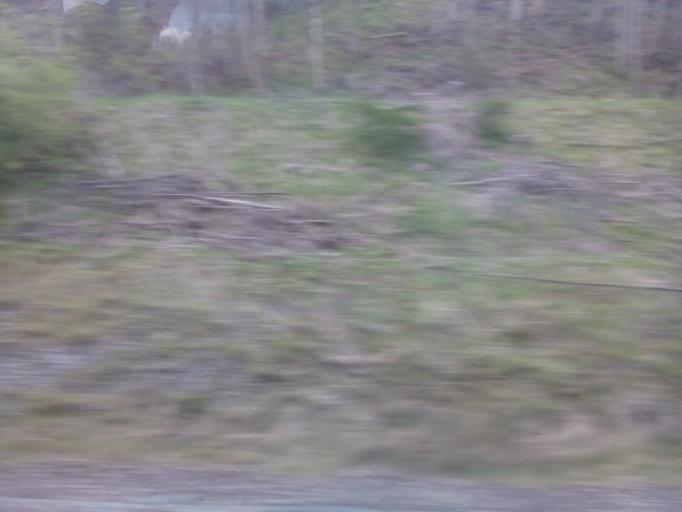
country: GB
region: England
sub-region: County Durham
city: Durham
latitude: 54.8004
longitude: -1.5607
